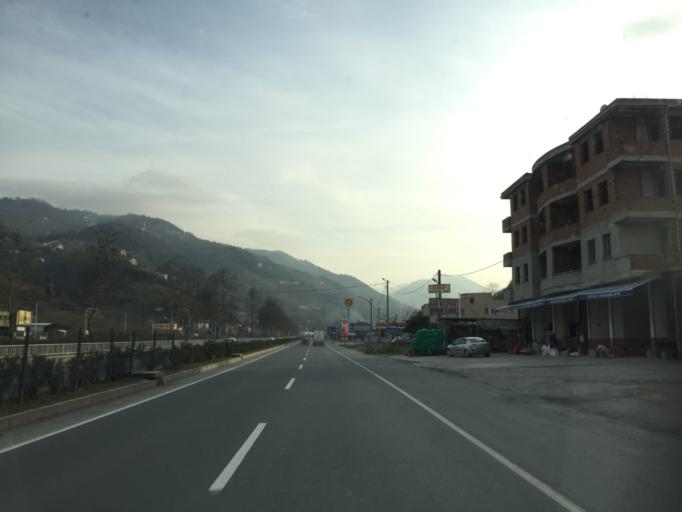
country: TR
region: Trabzon
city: Caglayan
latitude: 40.9113
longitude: 39.7196
